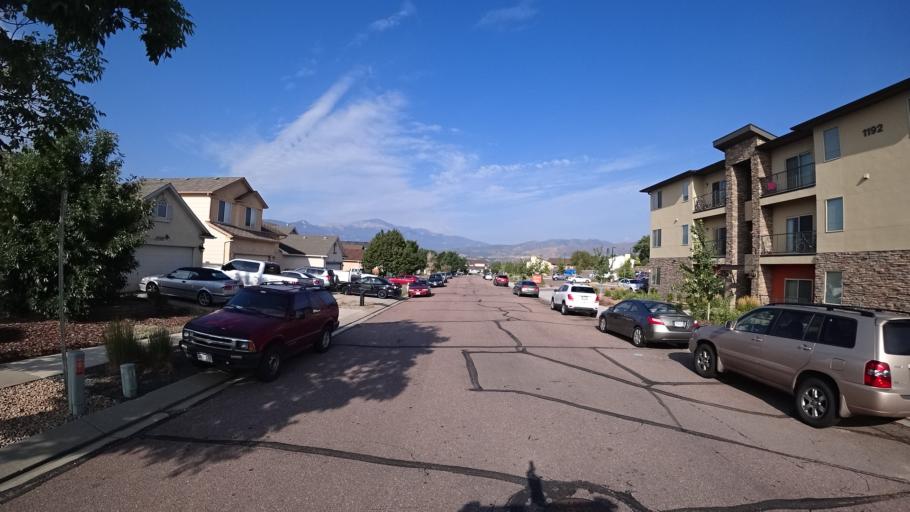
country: US
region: Colorado
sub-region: El Paso County
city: Colorado Springs
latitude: 38.8859
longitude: -104.8036
